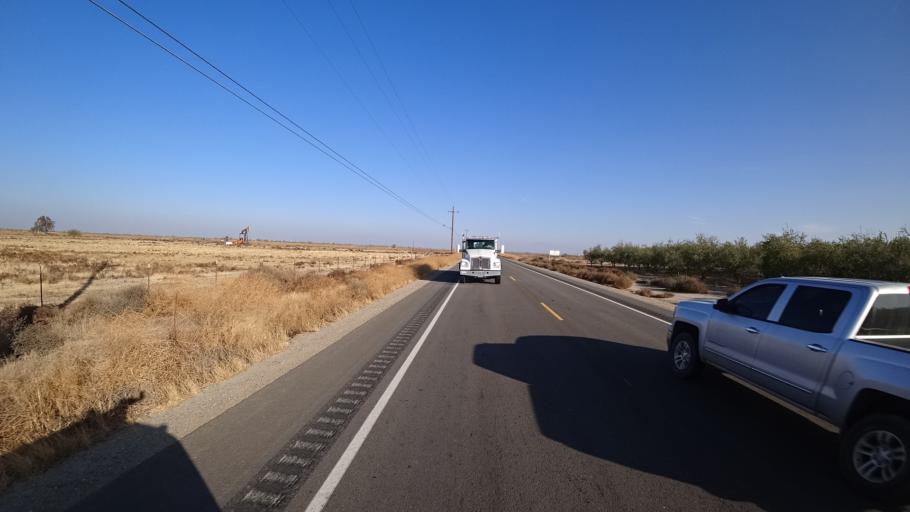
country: US
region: California
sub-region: Kern County
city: Rosedale
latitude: 35.2961
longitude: -119.2400
